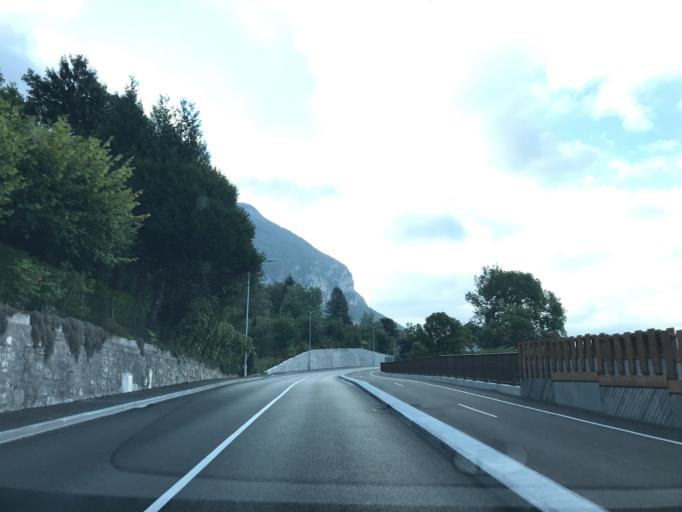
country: FR
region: Rhone-Alpes
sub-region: Departement de la Haute-Savoie
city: Veyrier-du-Lac
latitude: 45.8901
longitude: 6.1723
